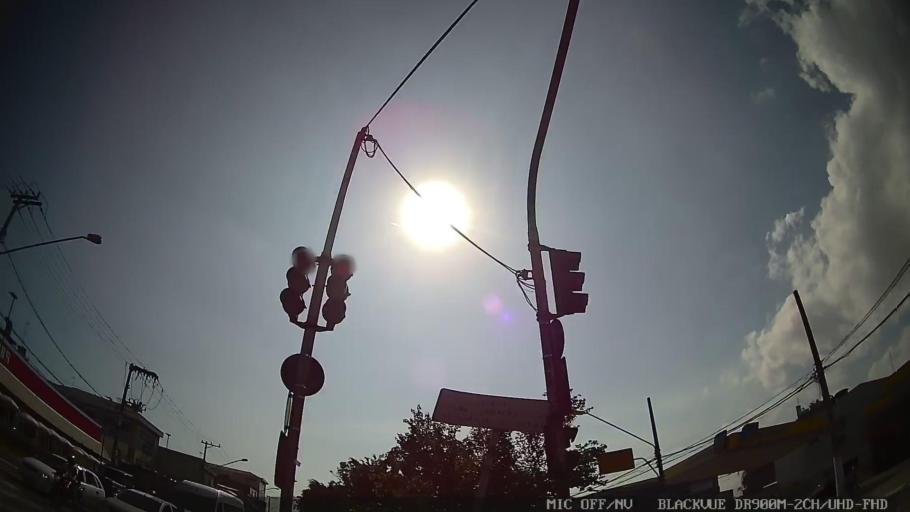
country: BR
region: Sao Paulo
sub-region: Ferraz De Vasconcelos
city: Ferraz de Vasconcelos
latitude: -23.5133
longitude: -46.4439
